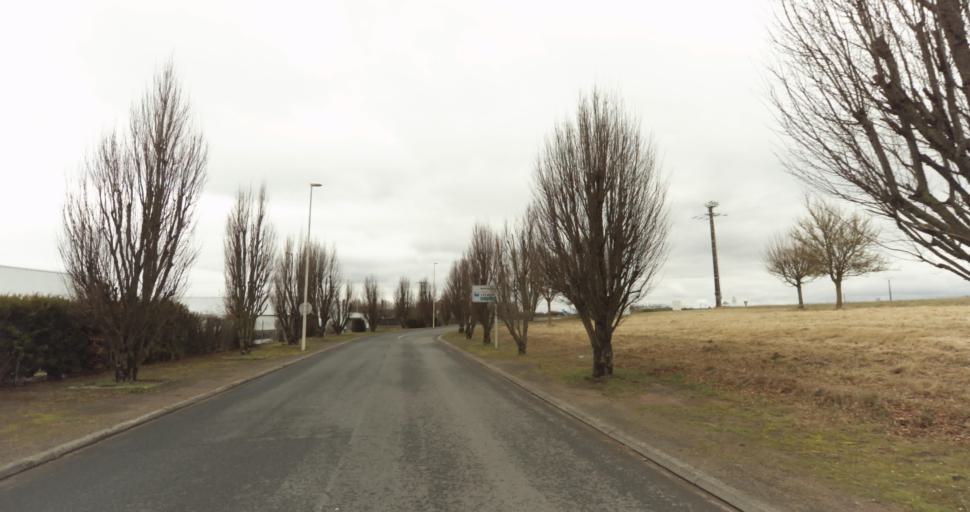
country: FR
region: Pays de la Loire
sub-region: Departement de Maine-et-Loire
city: Varrains
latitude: 47.2130
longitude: -0.0597
